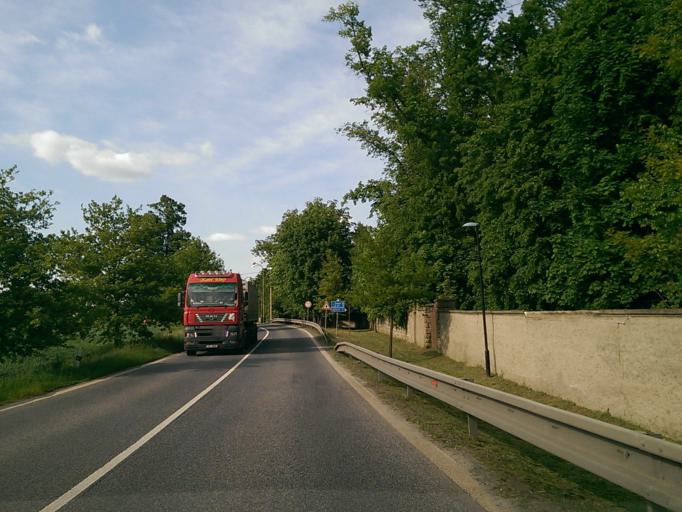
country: CZ
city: Duba
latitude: 50.5484
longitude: 14.5432
